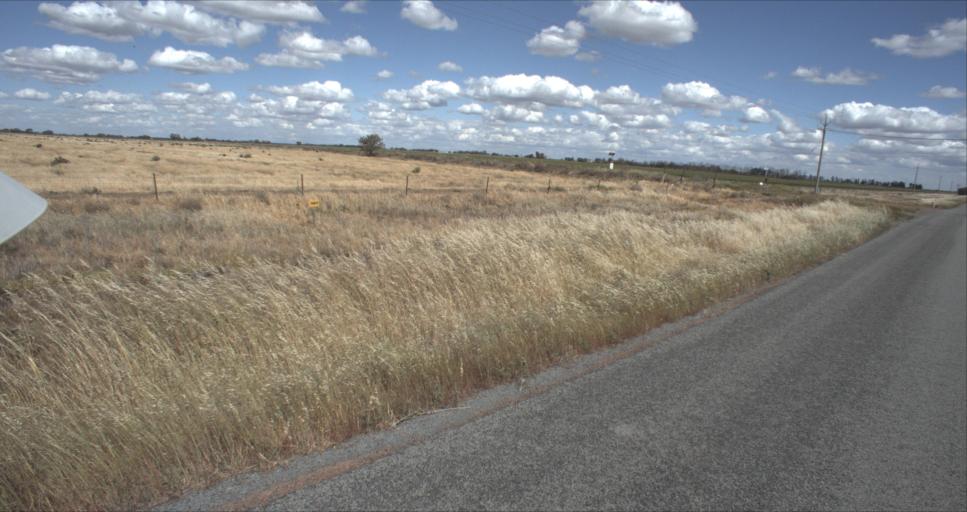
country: AU
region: New South Wales
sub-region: Leeton
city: Leeton
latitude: -34.4973
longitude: 146.2461
